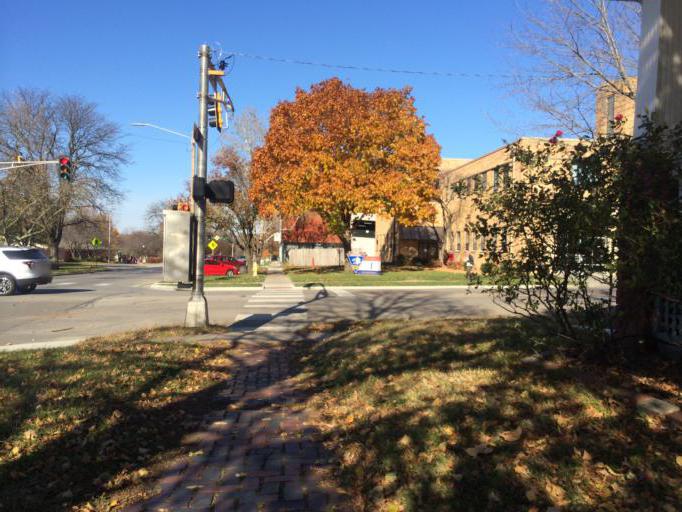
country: US
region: Kansas
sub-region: Douglas County
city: Lawrence
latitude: 38.9692
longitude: -95.2381
